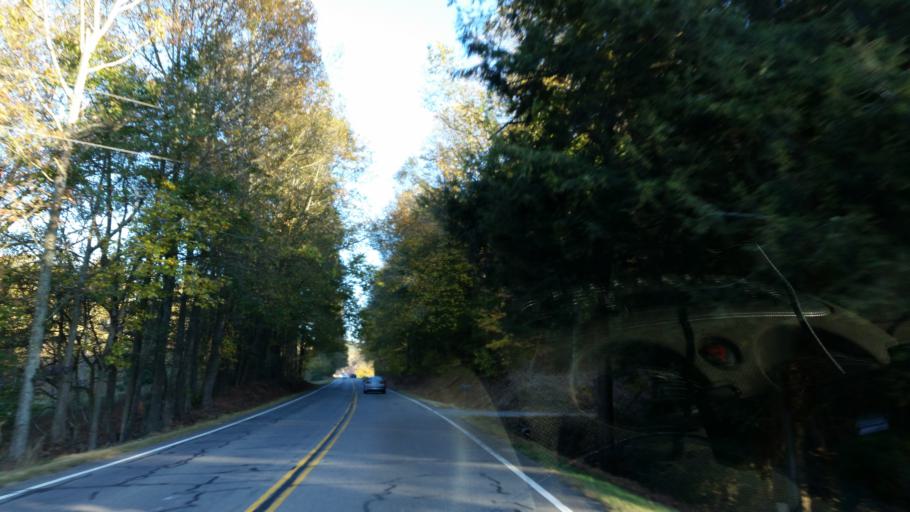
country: US
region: Georgia
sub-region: Pickens County
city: Jasper
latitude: 34.6029
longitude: -84.3459
